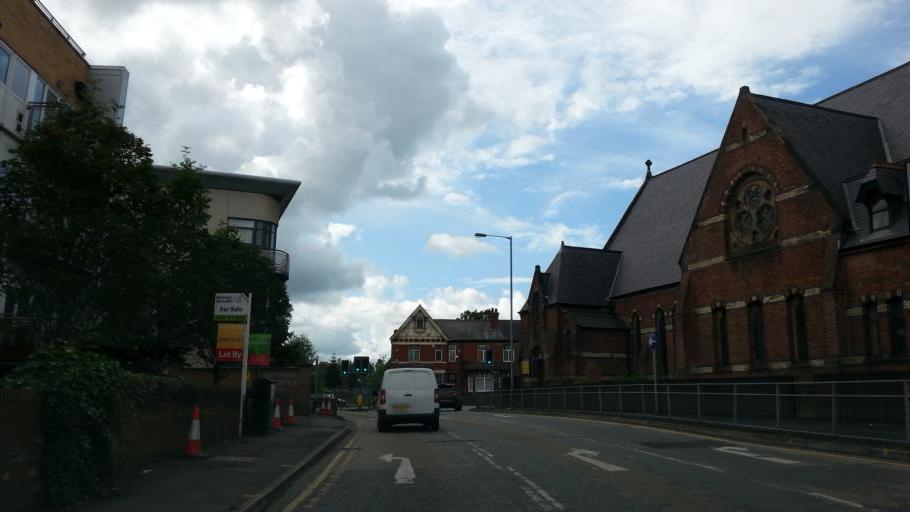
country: GB
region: England
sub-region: Borough of Bury
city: Prestwich
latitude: 53.5427
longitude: -2.2893
